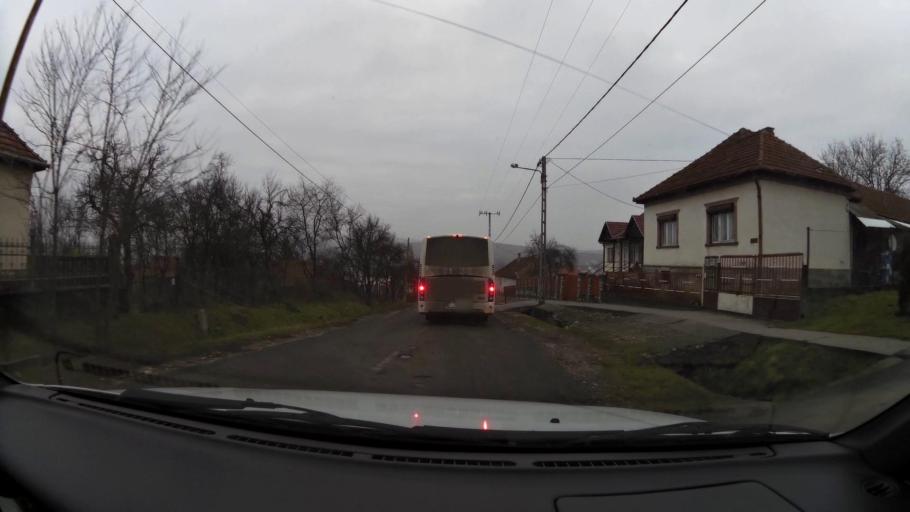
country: HU
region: Borsod-Abauj-Zemplen
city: Rudabanya
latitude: 48.4064
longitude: 20.6329
